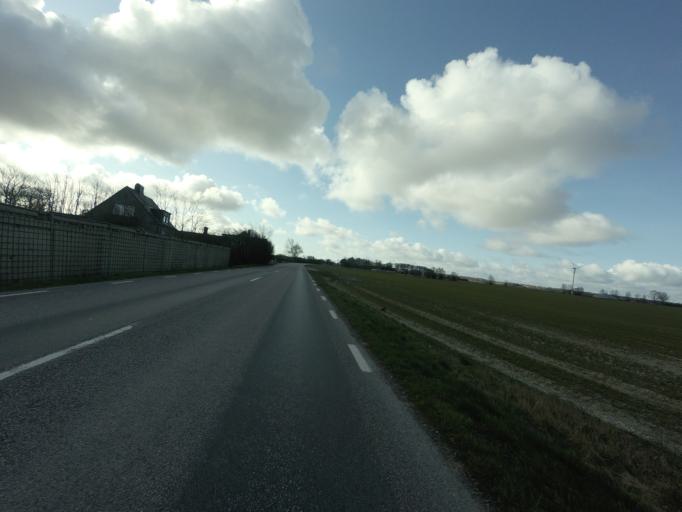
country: SE
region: Skane
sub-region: Helsingborg
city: Odakra
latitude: 56.1564
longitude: 12.6789
